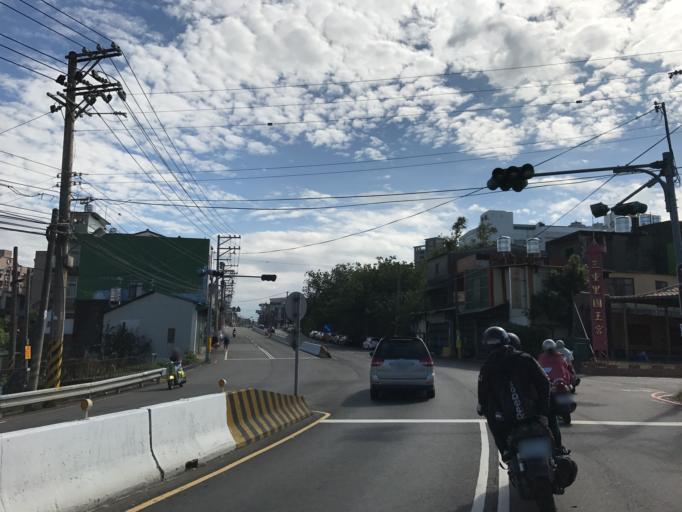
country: TW
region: Taiwan
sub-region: Hsinchu
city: Zhubei
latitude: 24.7606
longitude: 121.0616
